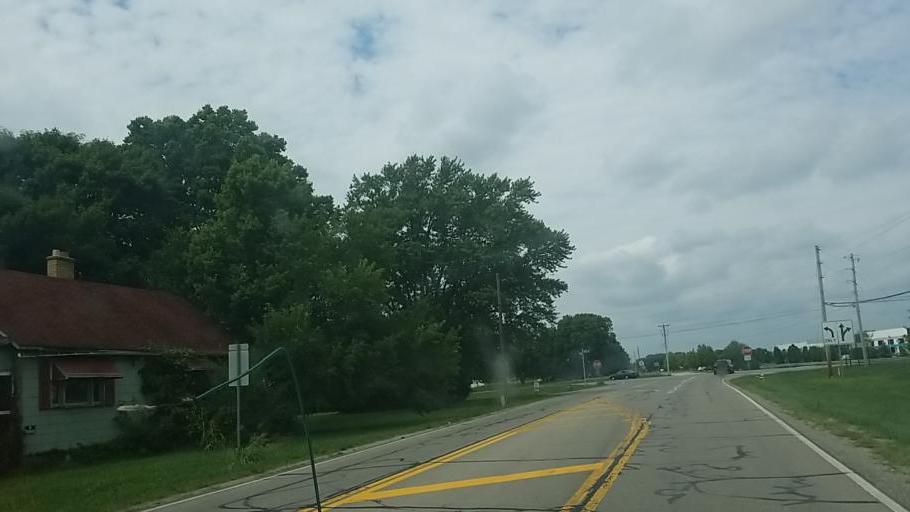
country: US
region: Ohio
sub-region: Franklin County
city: Groveport
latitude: 39.8388
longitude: -82.9037
